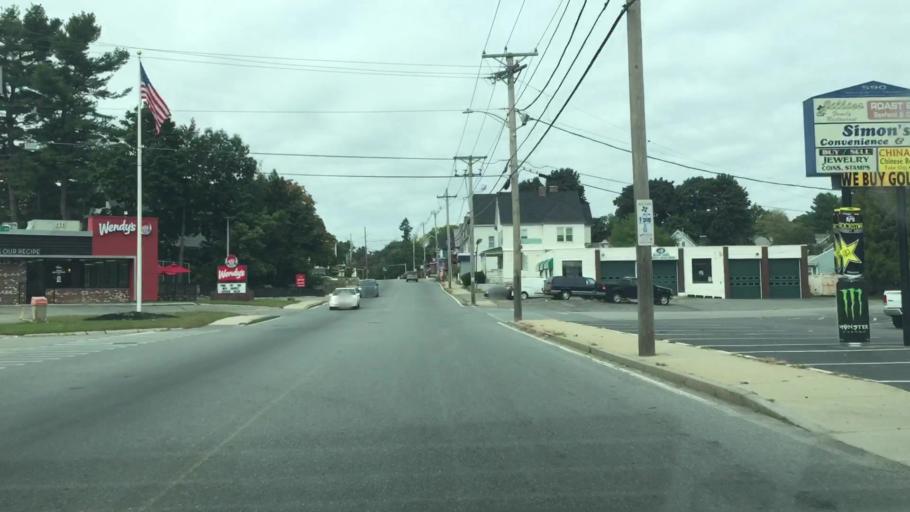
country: US
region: Massachusetts
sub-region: Middlesex County
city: Lowell
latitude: 42.6314
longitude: -71.2834
